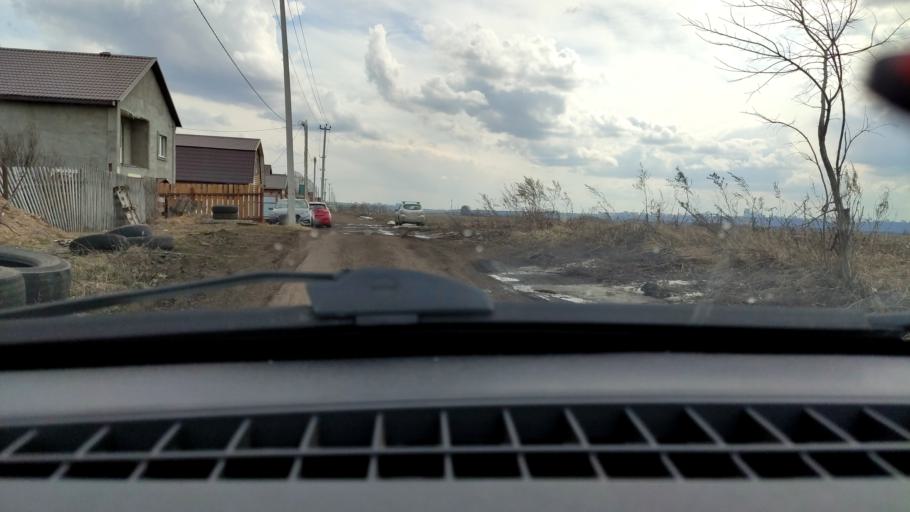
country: RU
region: Bashkortostan
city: Mikhaylovka
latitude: 54.8343
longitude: 55.9474
